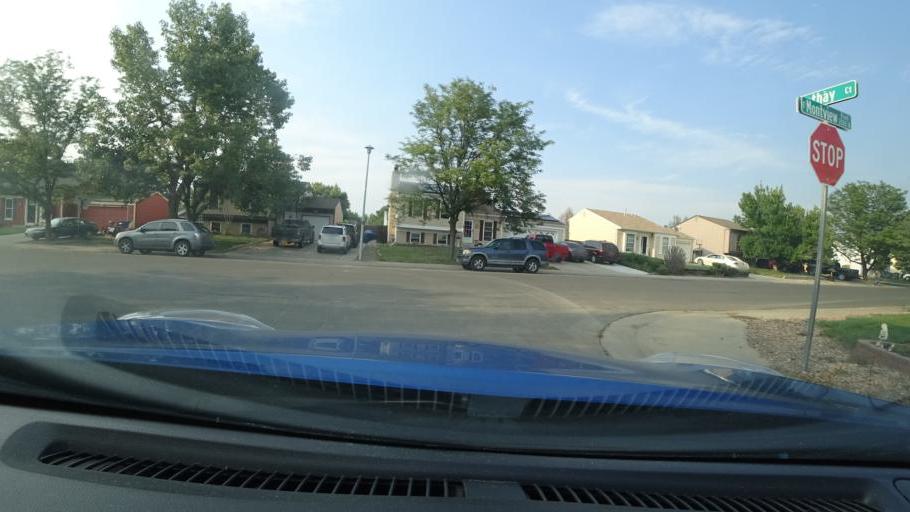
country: US
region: Colorado
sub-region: Adams County
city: Aurora
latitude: 39.7470
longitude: -104.7660
